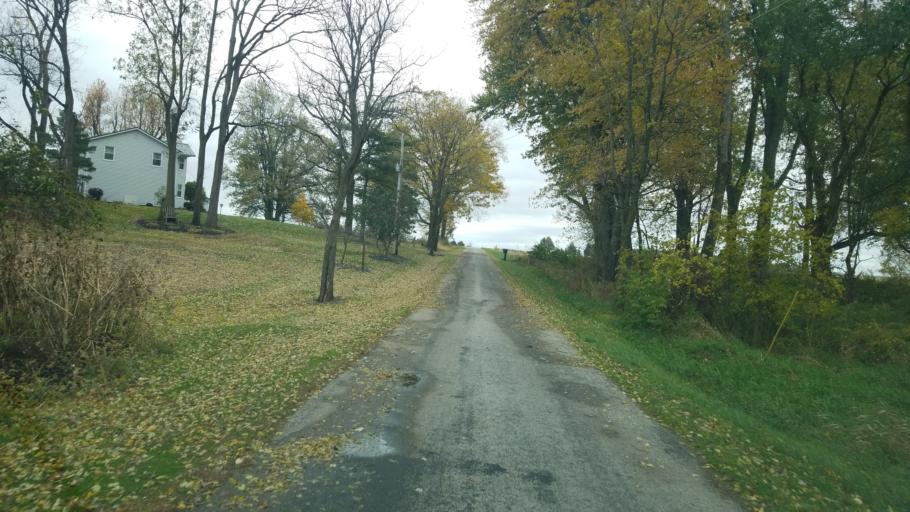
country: US
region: Ohio
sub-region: Crawford County
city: Bucyrus
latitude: 40.9072
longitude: -82.8654
